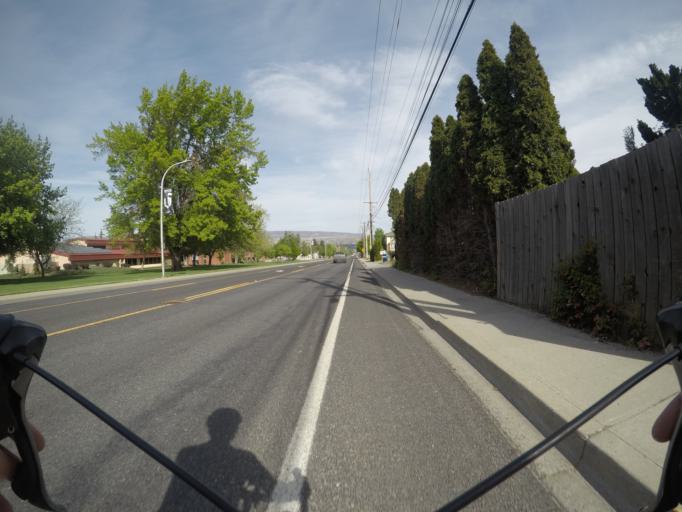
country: US
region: Washington
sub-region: Chelan County
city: West Wenatchee
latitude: 47.4298
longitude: -120.3380
